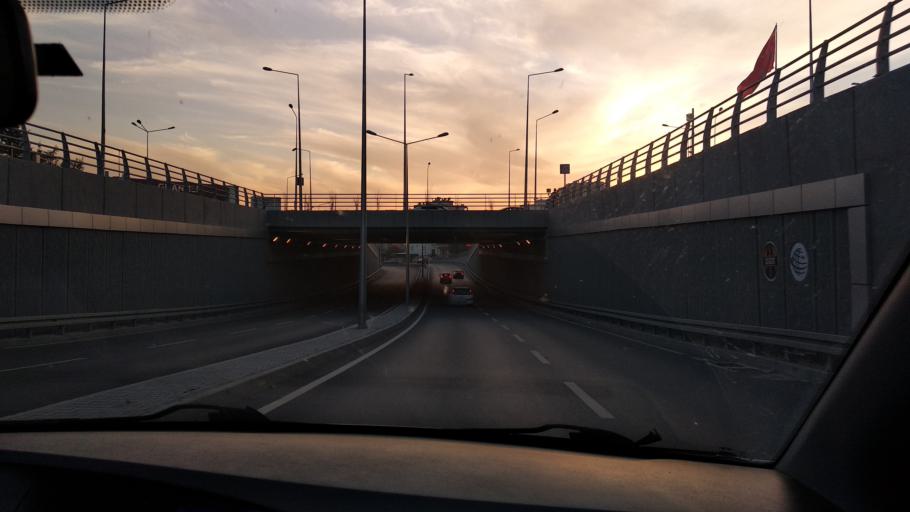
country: TR
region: Mersin
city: Mercin
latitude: 36.8207
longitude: 34.5983
